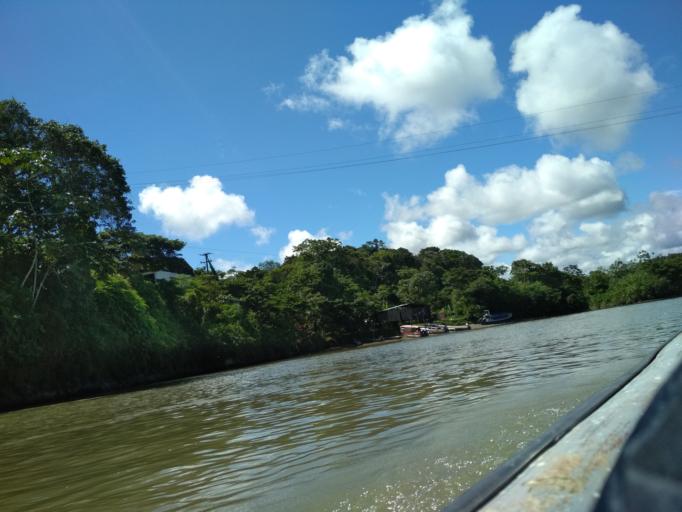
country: CO
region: Cauca
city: Timbiqui
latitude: 2.7697
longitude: -77.6635
